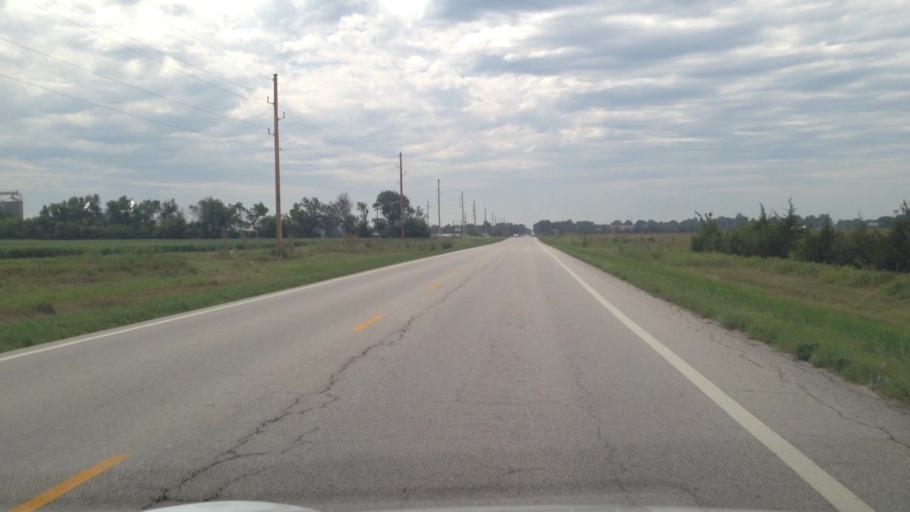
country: US
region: Kansas
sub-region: Allen County
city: Iola
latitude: 37.9314
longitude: -95.1701
